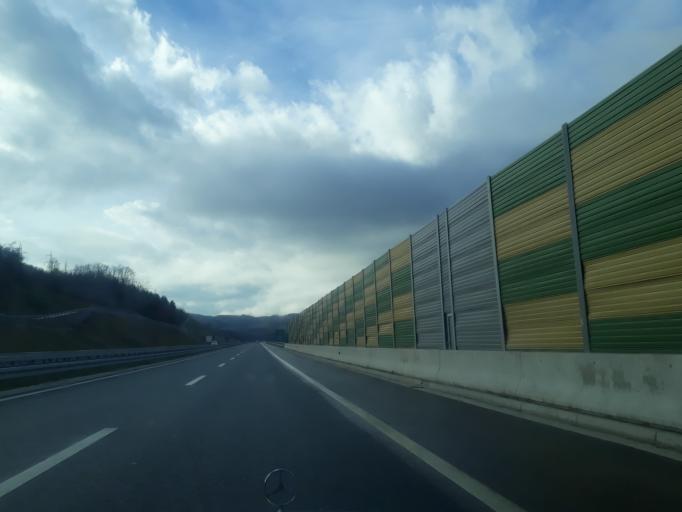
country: BA
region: Federation of Bosnia and Herzegovina
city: Polje
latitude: 43.8551
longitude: 18.1356
